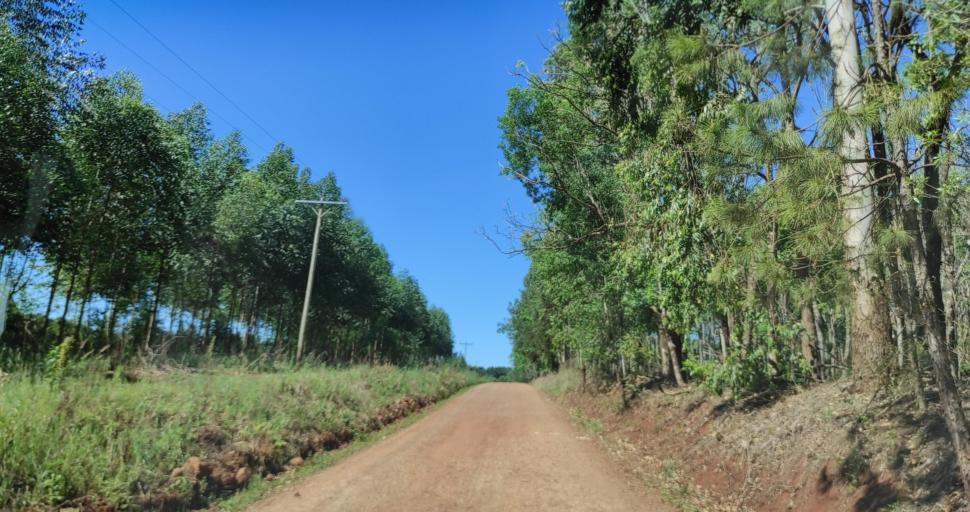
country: AR
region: Misiones
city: Capiovi
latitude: -26.9348
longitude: -55.0103
